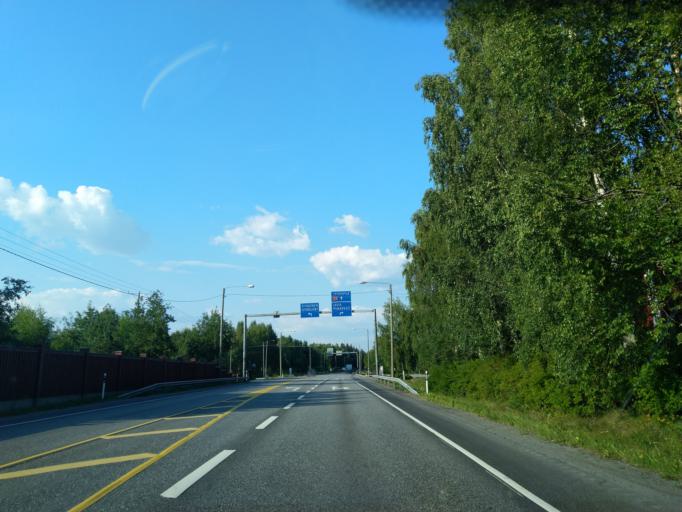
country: FI
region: Satakunta
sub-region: Pori
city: Pomarkku
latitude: 61.6989
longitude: 22.0094
